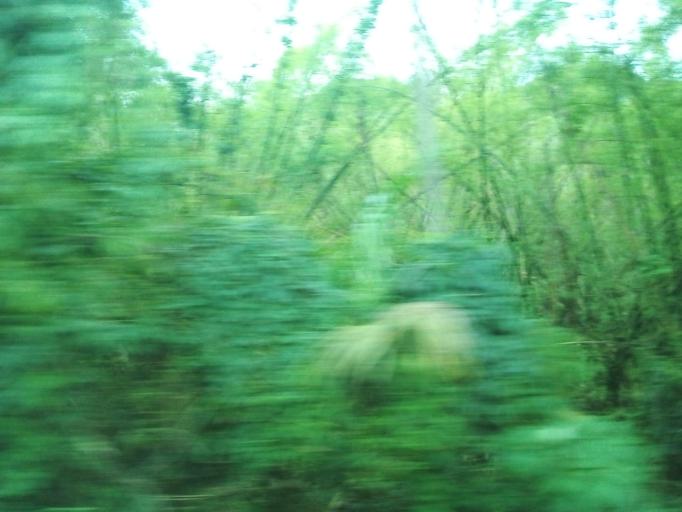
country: BR
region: Minas Gerais
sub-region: Nova Era
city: Nova Era
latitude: -19.7833
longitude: -43.0927
